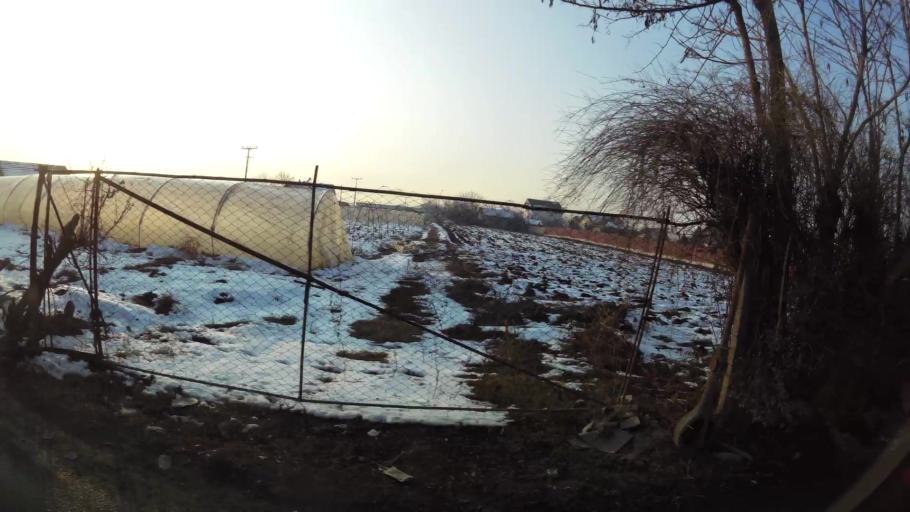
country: MK
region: Aracinovo
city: Arachinovo
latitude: 42.0138
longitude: 21.5259
